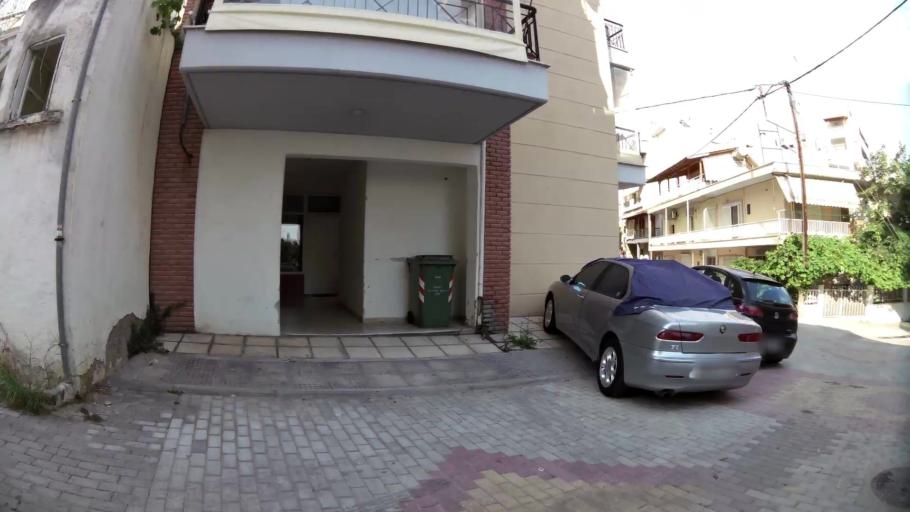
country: GR
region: Central Macedonia
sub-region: Nomos Thessalonikis
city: Sykies
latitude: 40.6587
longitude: 22.9578
